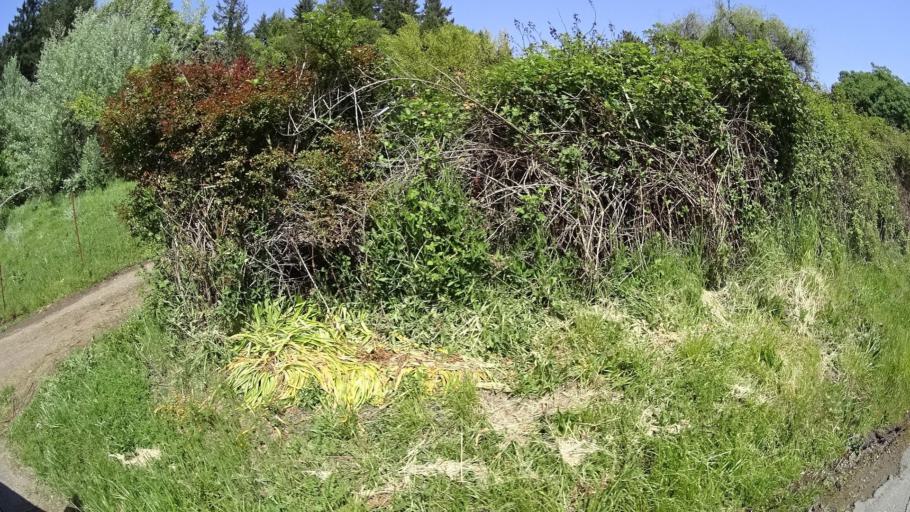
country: US
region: California
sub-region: Humboldt County
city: Redway
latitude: 40.2759
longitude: -123.6364
